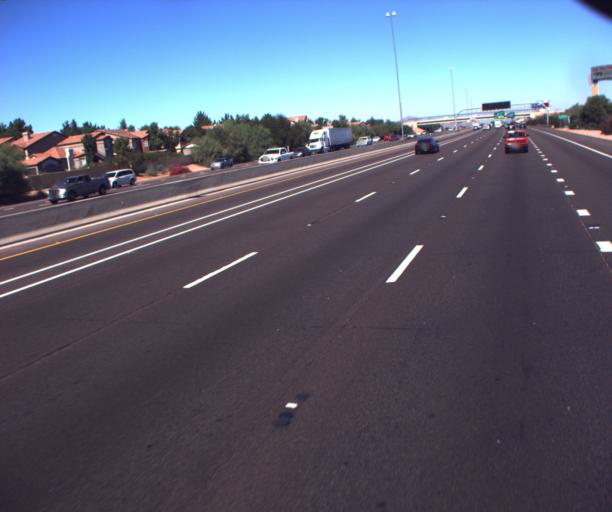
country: US
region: Arizona
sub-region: Maricopa County
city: Guadalupe
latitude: 33.3595
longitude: -111.9695
